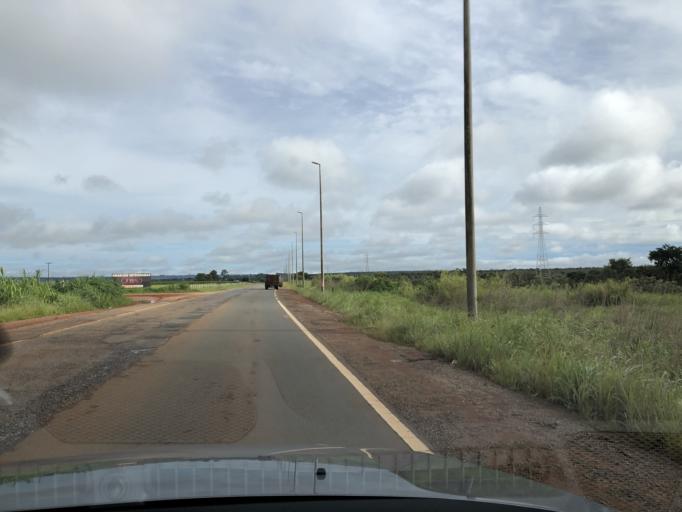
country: BR
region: Federal District
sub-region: Brasilia
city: Brasilia
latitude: -15.7233
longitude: -48.0866
